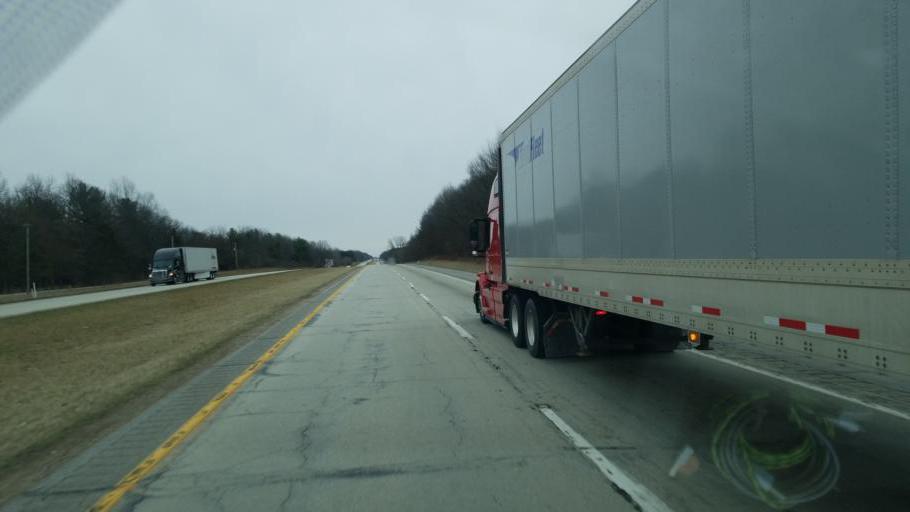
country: US
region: Indiana
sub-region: Starke County
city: Koontz Lake
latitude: 41.3644
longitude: -86.4590
